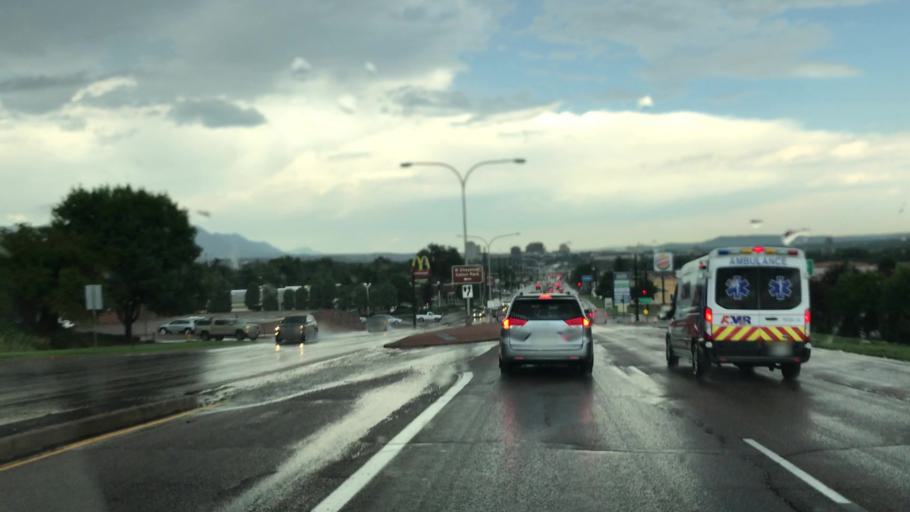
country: US
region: Colorado
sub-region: El Paso County
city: Colorado Springs
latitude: 38.8053
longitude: -104.8222
